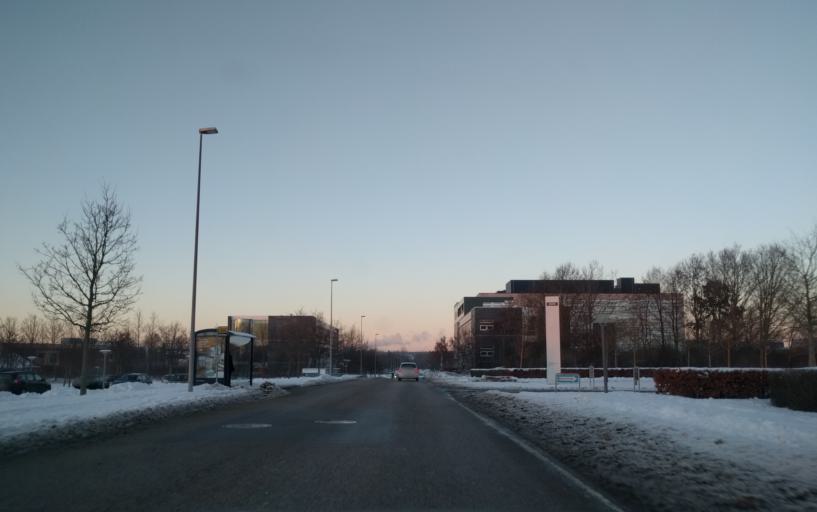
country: DK
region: North Denmark
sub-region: Alborg Kommune
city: Gistrup
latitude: 57.0129
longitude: 9.9841
